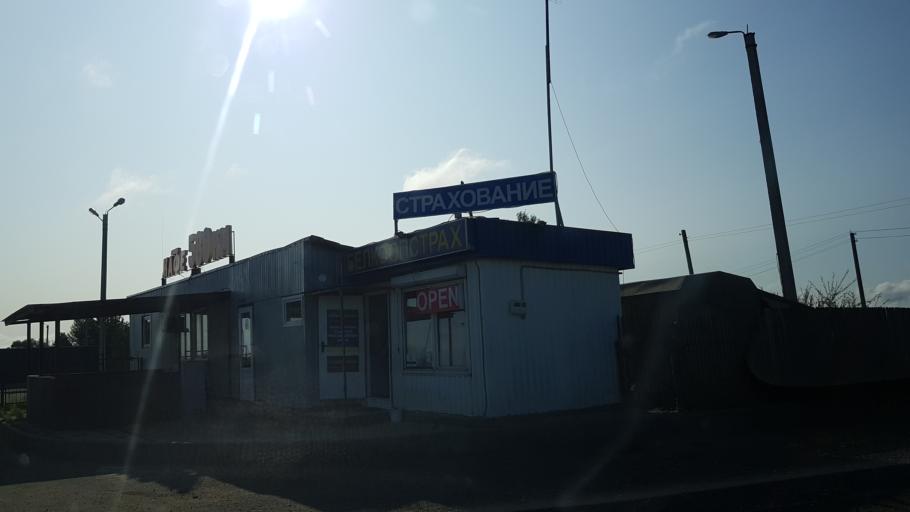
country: BY
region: Vitebsk
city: Dubrowna
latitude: 54.6348
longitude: 30.5331
